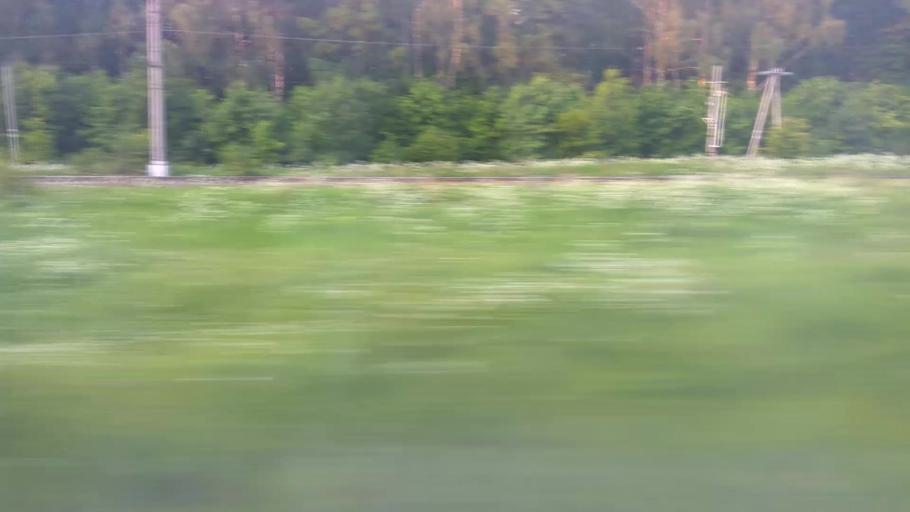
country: RU
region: Moskovskaya
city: Belyye Stolby
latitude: 55.3024
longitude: 37.8776
